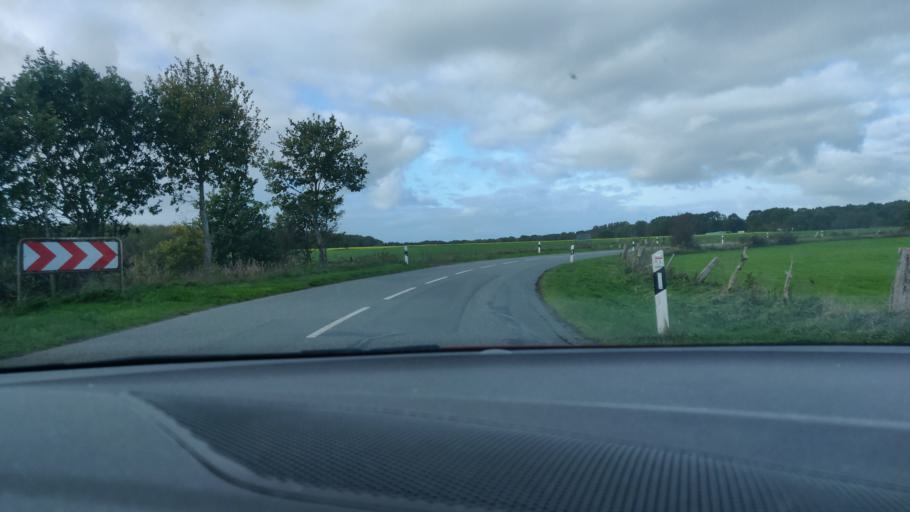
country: DE
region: Lower Saxony
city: Cuxhaven
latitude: 53.8335
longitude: 8.6630
